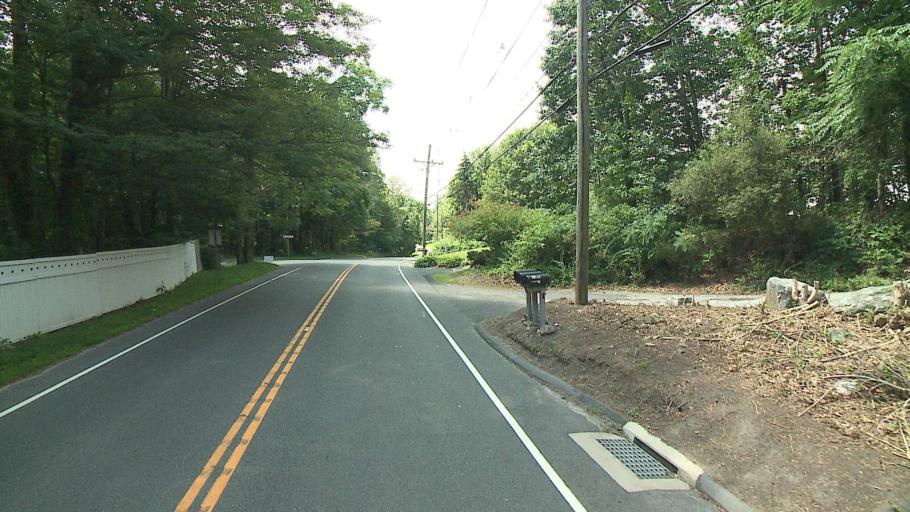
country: US
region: New York
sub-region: Putnam County
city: Putnam Lake
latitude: 41.4736
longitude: -73.4688
